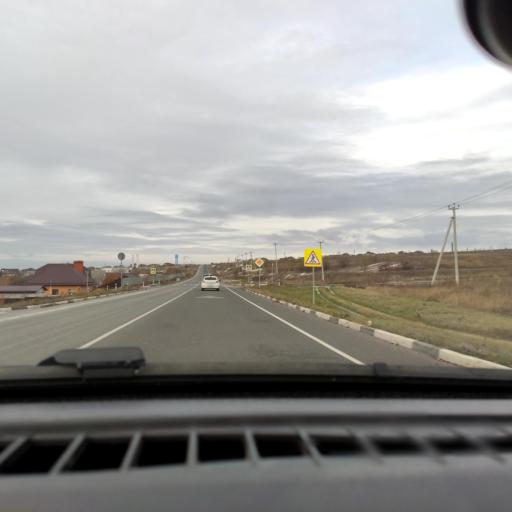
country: RU
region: Belgorod
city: Alekseyevka
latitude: 50.6435
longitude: 38.6479
